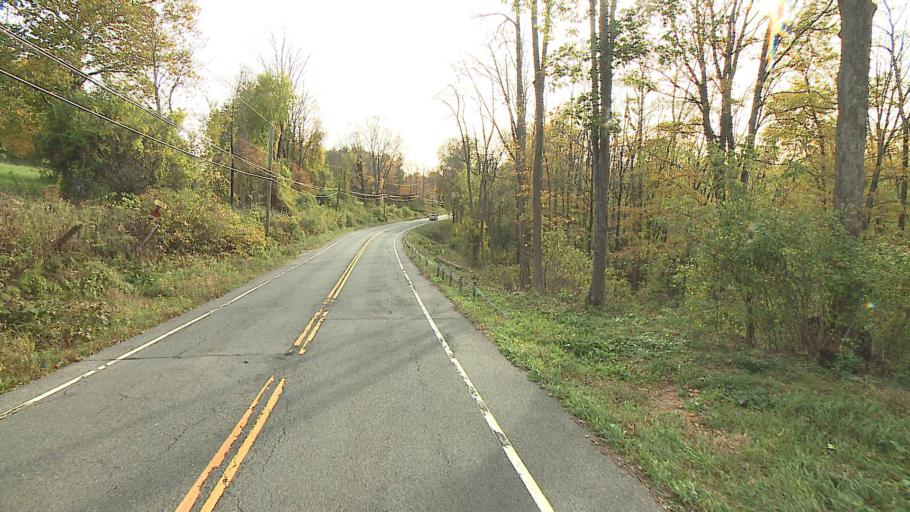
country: US
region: Connecticut
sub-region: Litchfield County
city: Canaan
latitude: 42.0080
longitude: -73.3548
